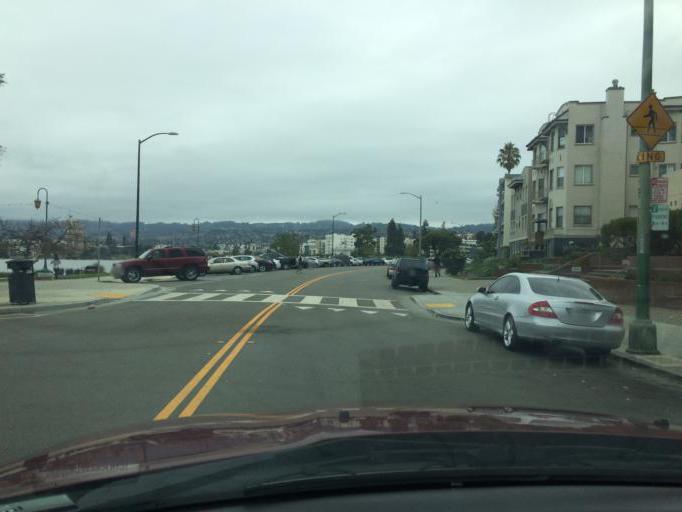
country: US
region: California
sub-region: Alameda County
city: Oakland
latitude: 37.7992
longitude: -122.2584
